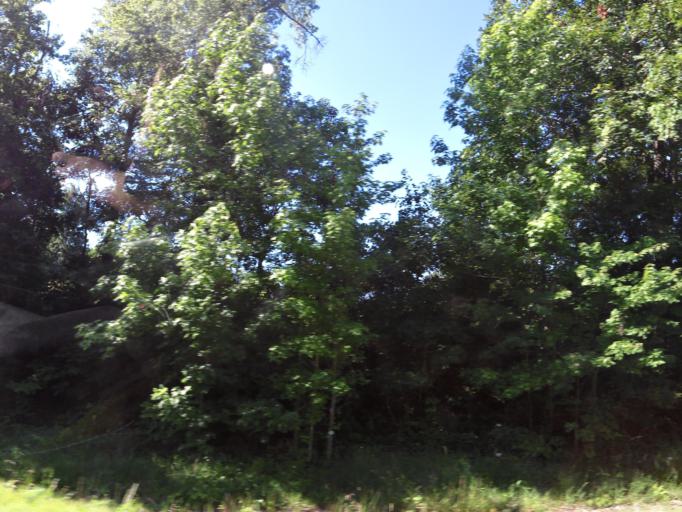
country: US
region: Arkansas
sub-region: Clay County
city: Piggott
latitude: 36.4336
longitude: -90.3282
